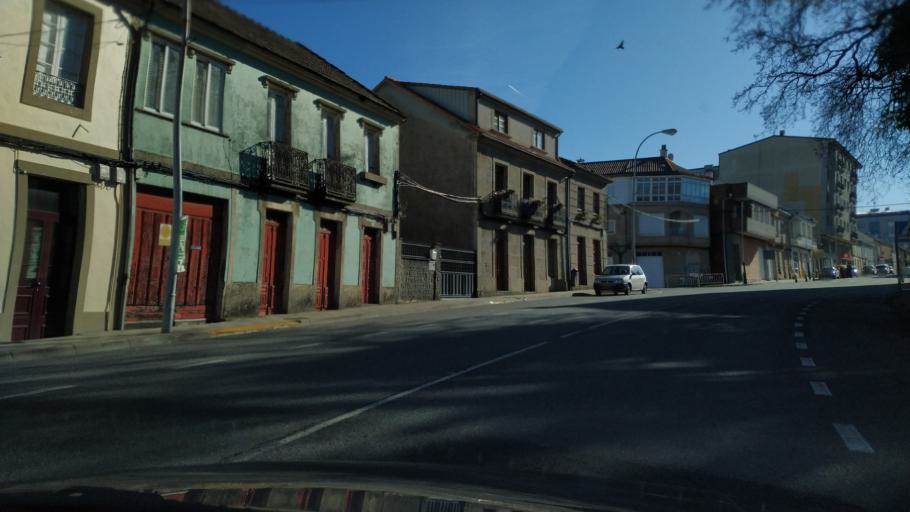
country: ES
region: Galicia
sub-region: Provincia de Pontevedra
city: Silleda
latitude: 42.7314
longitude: -8.3064
